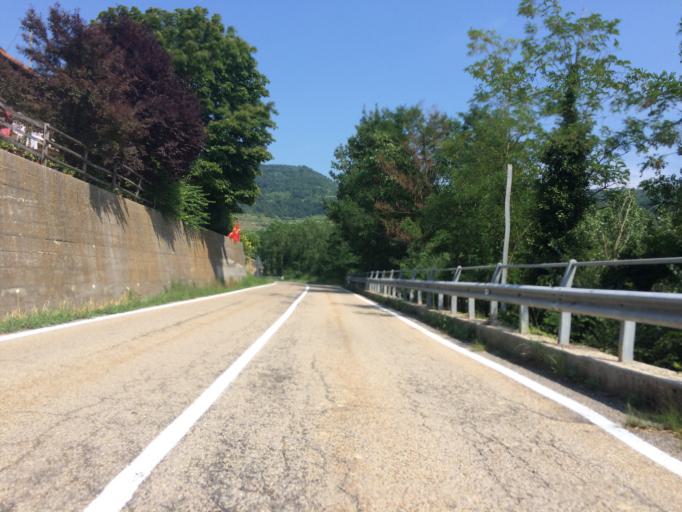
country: IT
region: Piedmont
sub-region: Provincia di Cuneo
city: Torre Bormida
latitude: 44.5599
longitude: 8.1617
